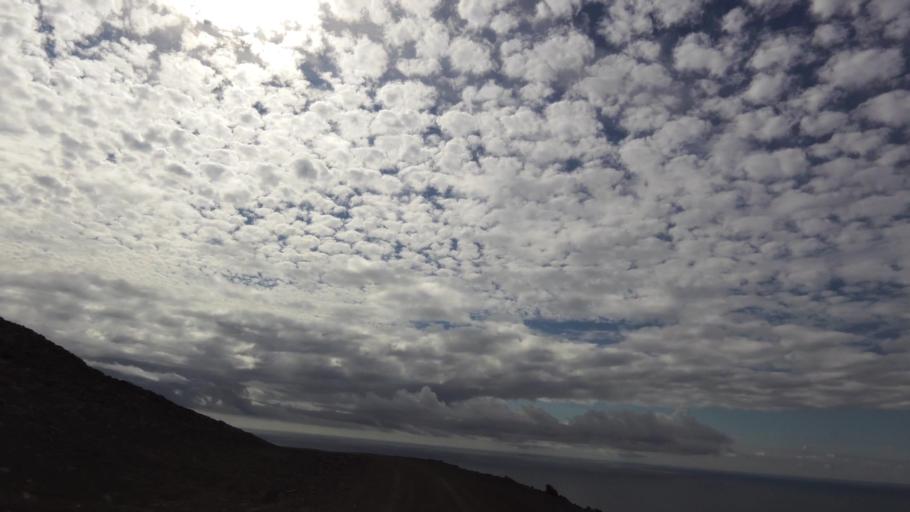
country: IS
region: West
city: Olafsvik
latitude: 65.6224
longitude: -24.2979
